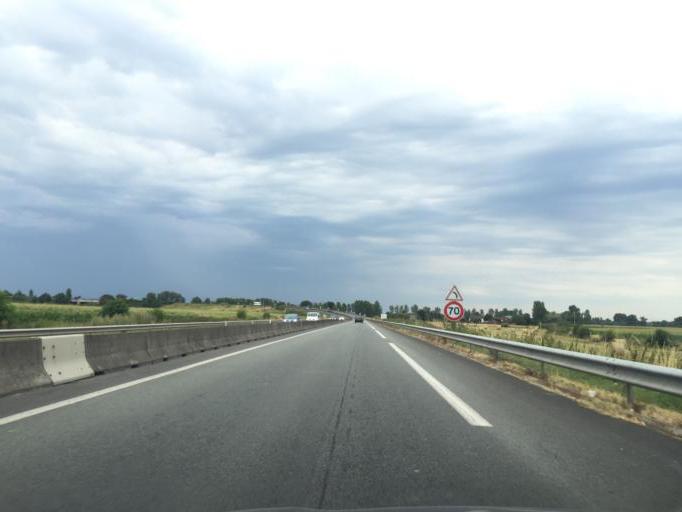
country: FR
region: Auvergne
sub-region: Departement de l'Allier
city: Toulon-sur-Allier
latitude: 46.5063
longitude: 3.3567
